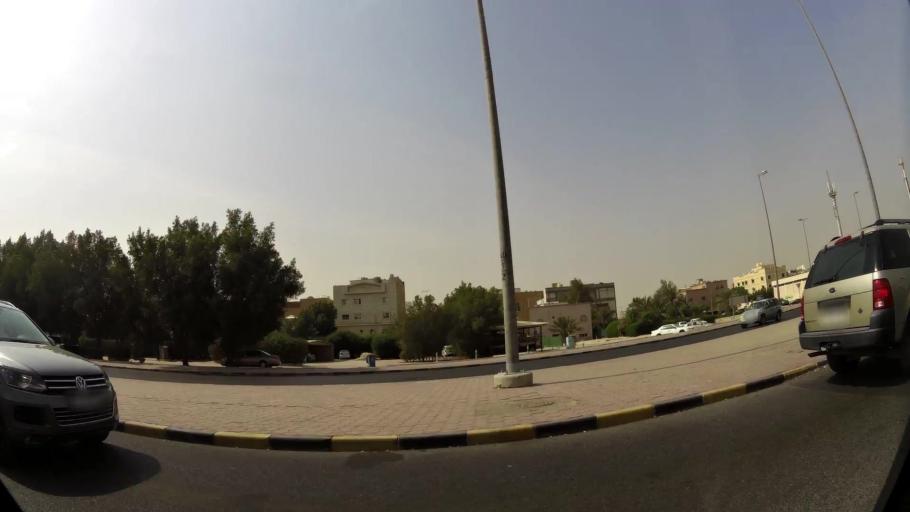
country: KW
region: Al Asimah
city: Ar Rabiyah
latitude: 29.2842
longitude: 47.9066
